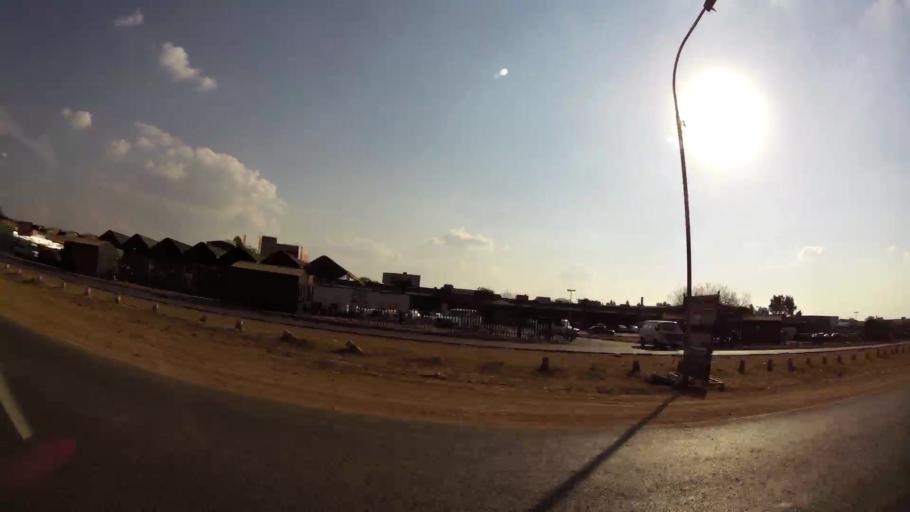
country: ZA
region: Gauteng
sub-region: Ekurhuleni Metropolitan Municipality
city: Tembisa
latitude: -25.9499
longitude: 28.2330
